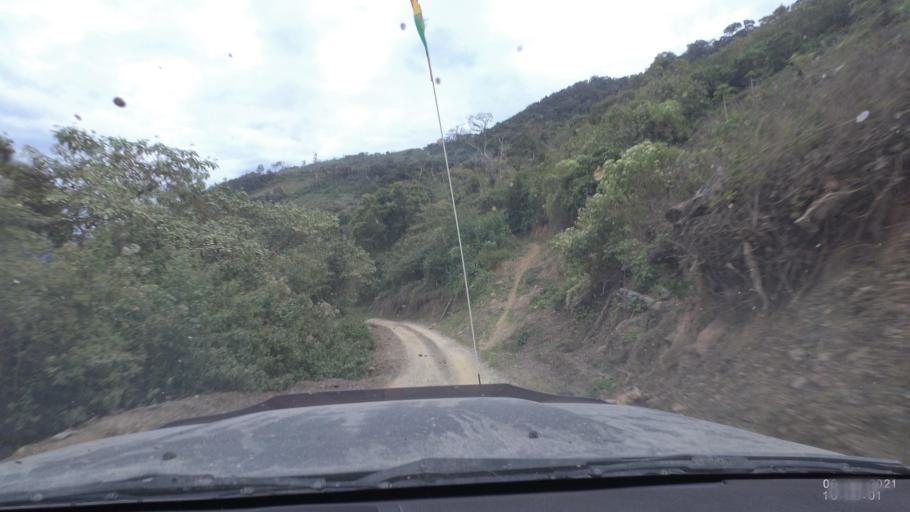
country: BO
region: La Paz
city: Quime
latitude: -16.5431
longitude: -66.7513
